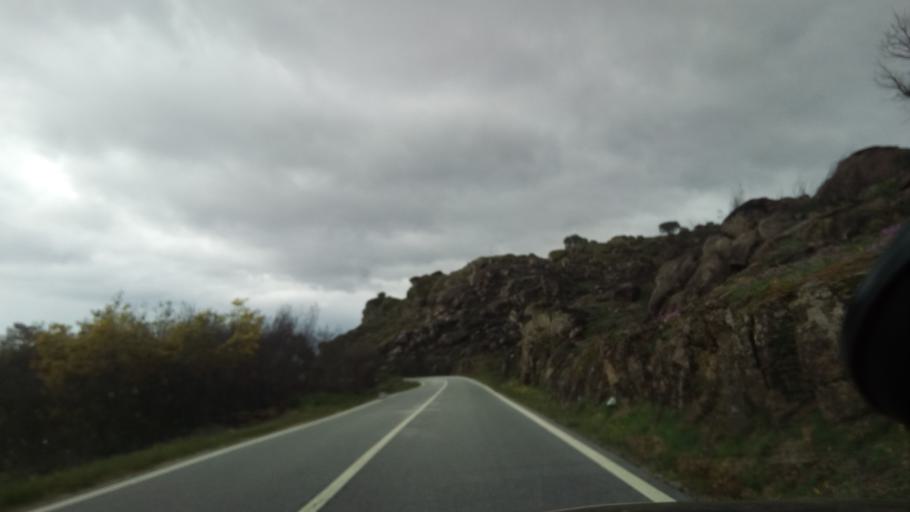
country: PT
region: Guarda
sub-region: Fornos de Algodres
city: Fornos de Algodres
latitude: 40.5620
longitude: -7.5597
